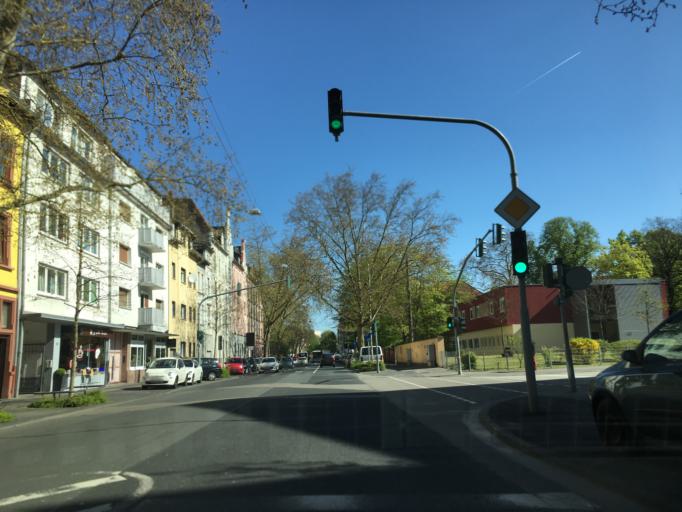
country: DE
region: Hesse
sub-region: Regierungsbezirk Darmstadt
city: Offenbach
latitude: 50.0946
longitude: 8.7534
